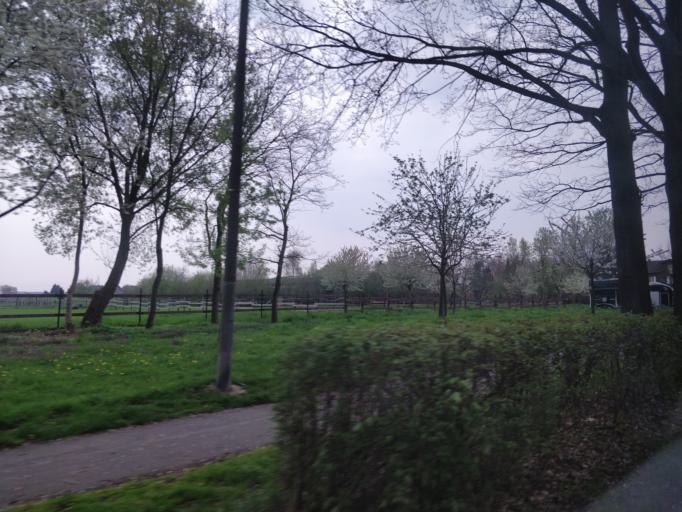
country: DE
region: North Rhine-Westphalia
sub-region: Regierungsbezirk Koln
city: Pulheim
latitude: 50.9634
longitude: 6.8248
